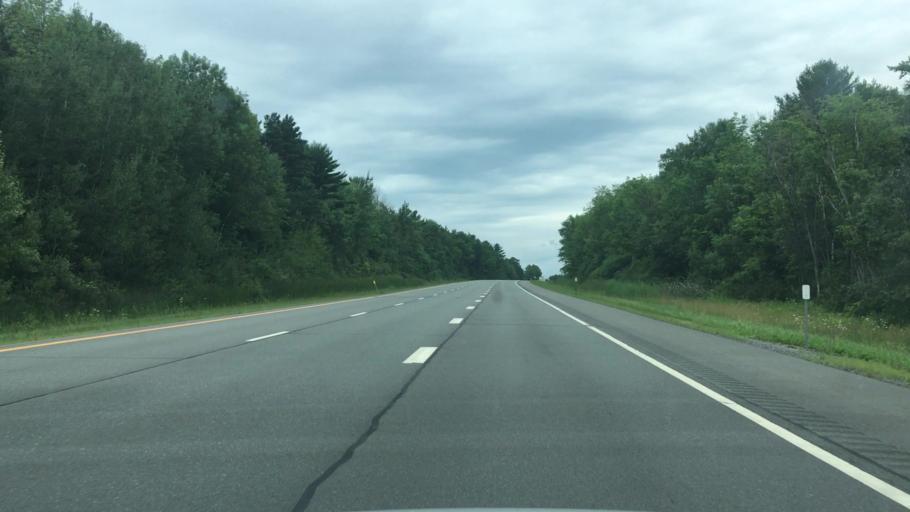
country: US
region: New York
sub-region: Schoharie County
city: Schoharie
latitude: 42.7257
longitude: -74.2181
